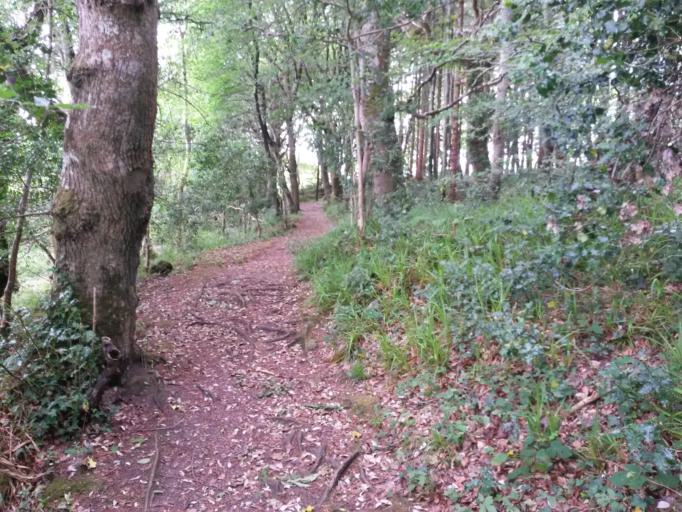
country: IE
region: Connaught
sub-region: Sligo
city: Sligo
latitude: 54.2402
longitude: -8.4297
